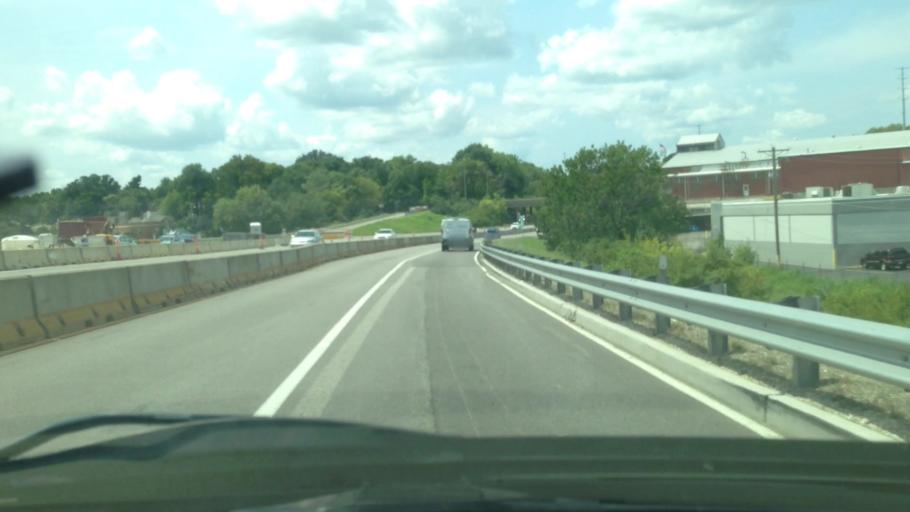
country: US
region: Missouri
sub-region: Saint Louis County
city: Shrewsbury
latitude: 38.5957
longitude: -90.3233
